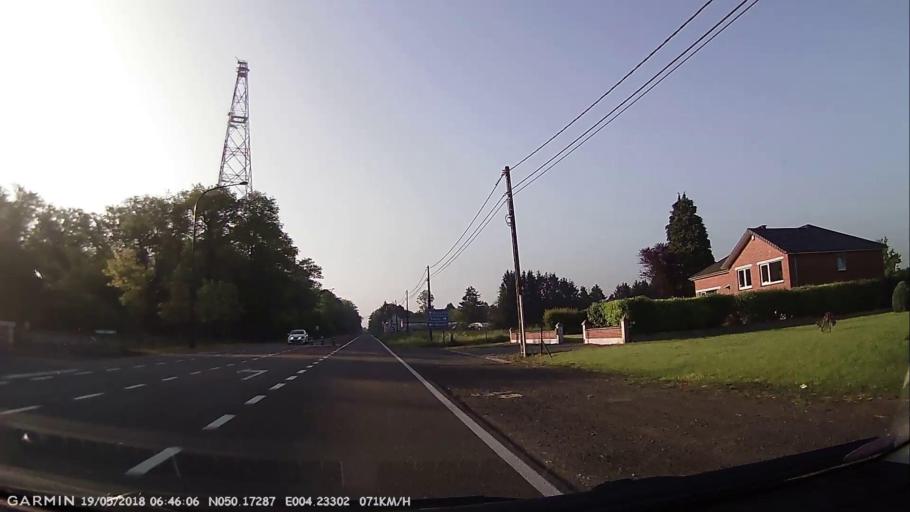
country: BE
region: Wallonia
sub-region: Province du Hainaut
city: Beaumont
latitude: 50.1728
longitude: 4.2331
